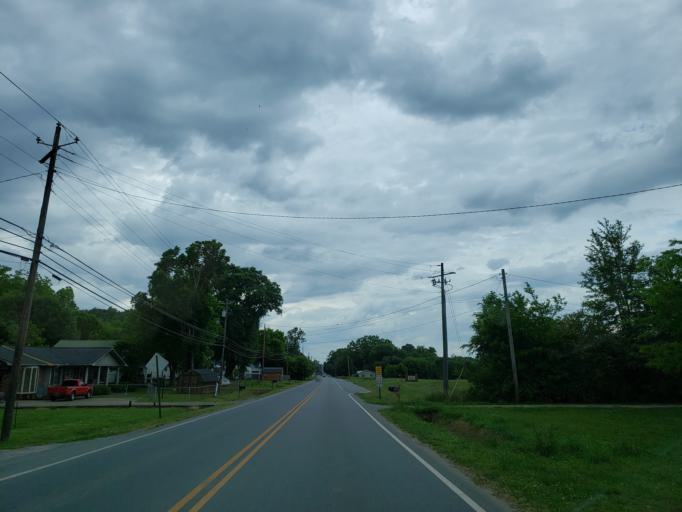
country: US
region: Georgia
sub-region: Polk County
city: Rockmart
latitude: 33.9880
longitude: -85.0416
